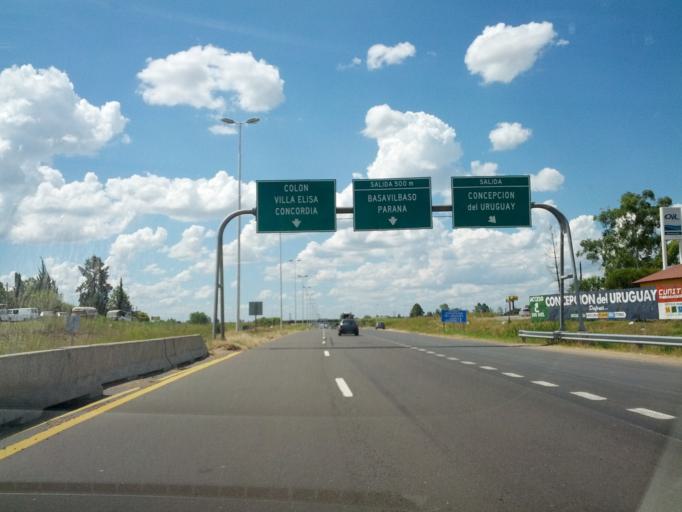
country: AR
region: Entre Rios
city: Concepcion del Uruguay
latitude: -32.4916
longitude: -58.3116
